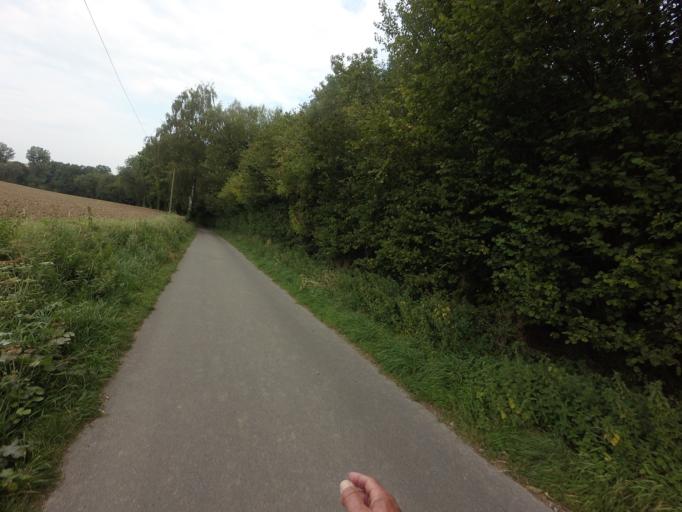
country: NL
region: Limburg
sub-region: Gemeente Simpelveld
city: Simpelveld
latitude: 50.8024
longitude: 5.9888
